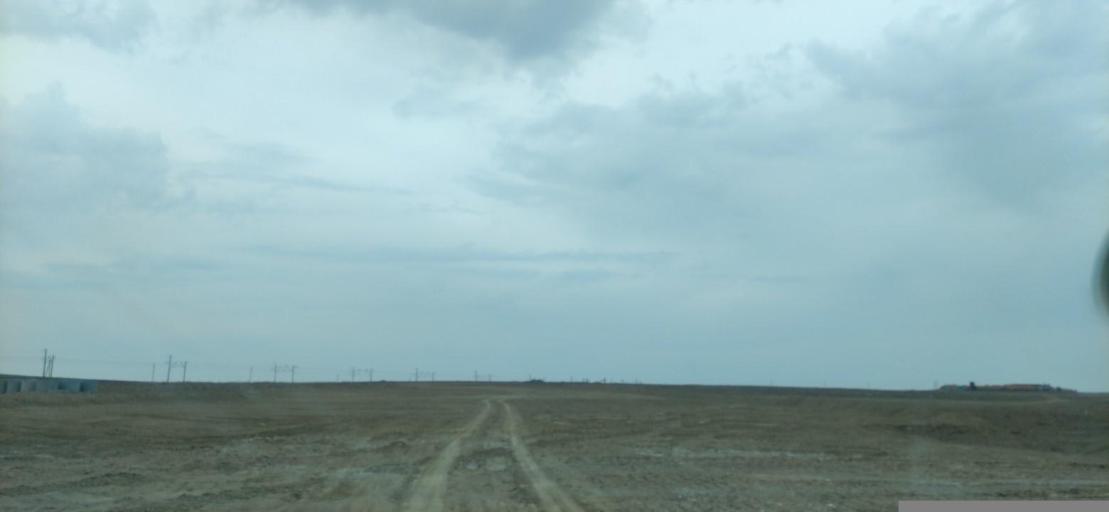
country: KZ
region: Qaraghandy
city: Saryshaghan
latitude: 46.0917
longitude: 73.6059
